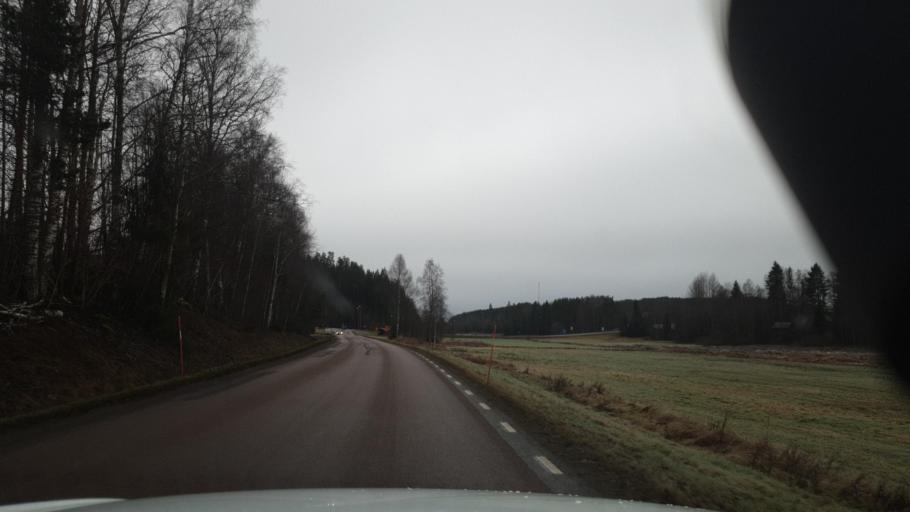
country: SE
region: Vaermland
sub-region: Arvika Kommun
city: Arvika
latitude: 59.6707
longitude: 12.7970
